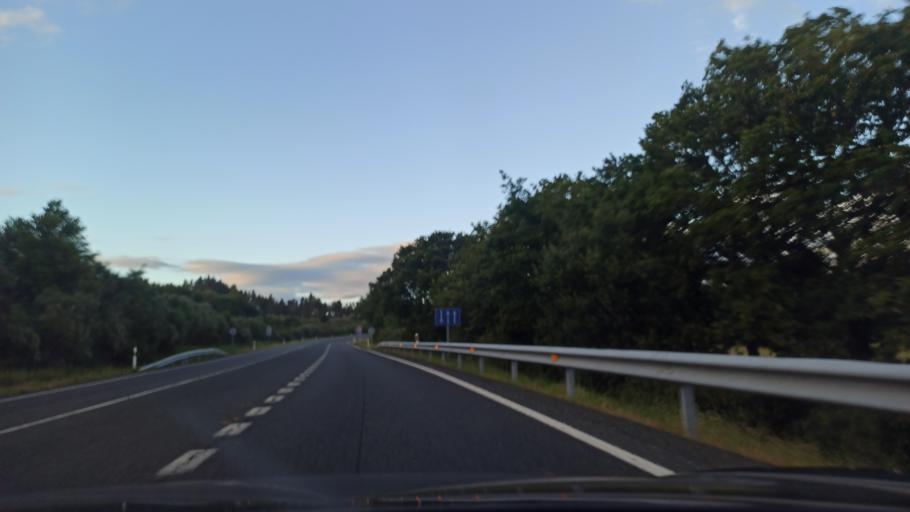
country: ES
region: Galicia
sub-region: Provincia de Pontevedra
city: Rodeiro
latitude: 42.7691
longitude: -7.9727
